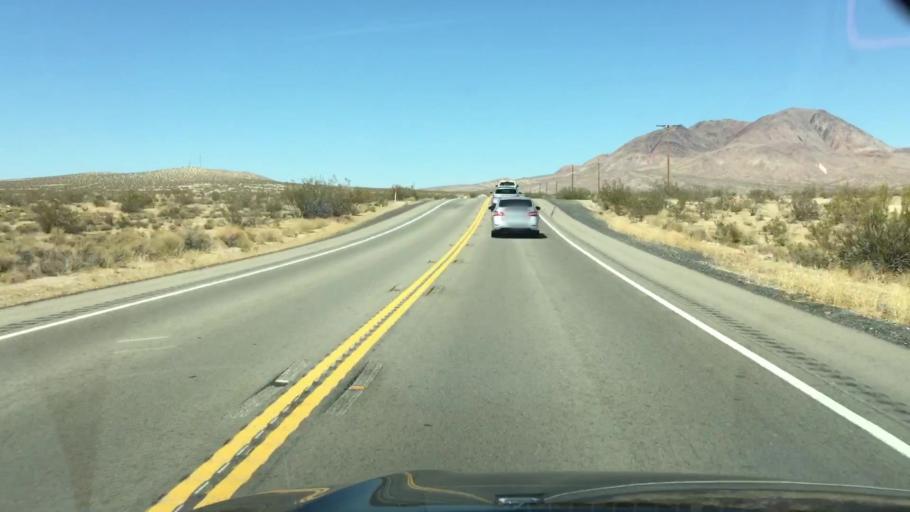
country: US
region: California
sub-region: Kern County
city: Boron
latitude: 35.2998
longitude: -117.6136
